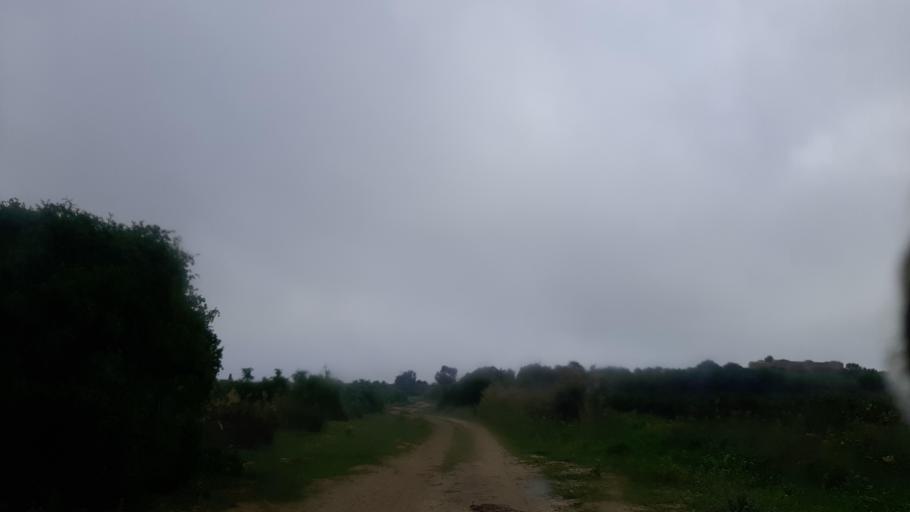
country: TN
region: Nabul
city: Qulaybiyah
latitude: 36.8241
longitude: 11.0447
